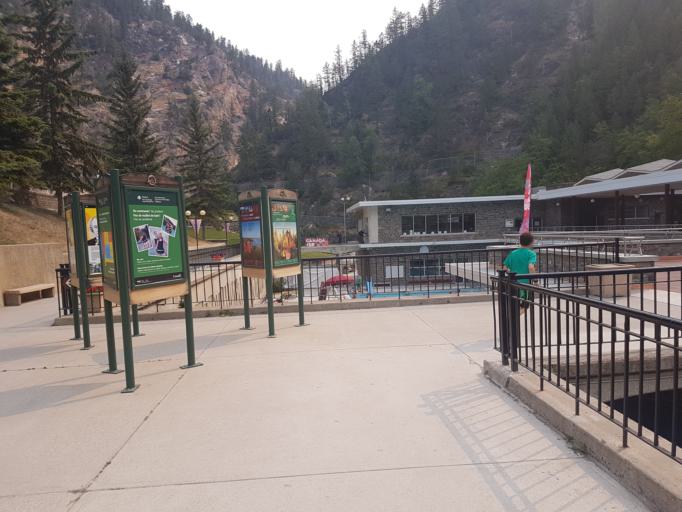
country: CA
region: British Columbia
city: Invermere
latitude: 50.6348
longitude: -116.0398
